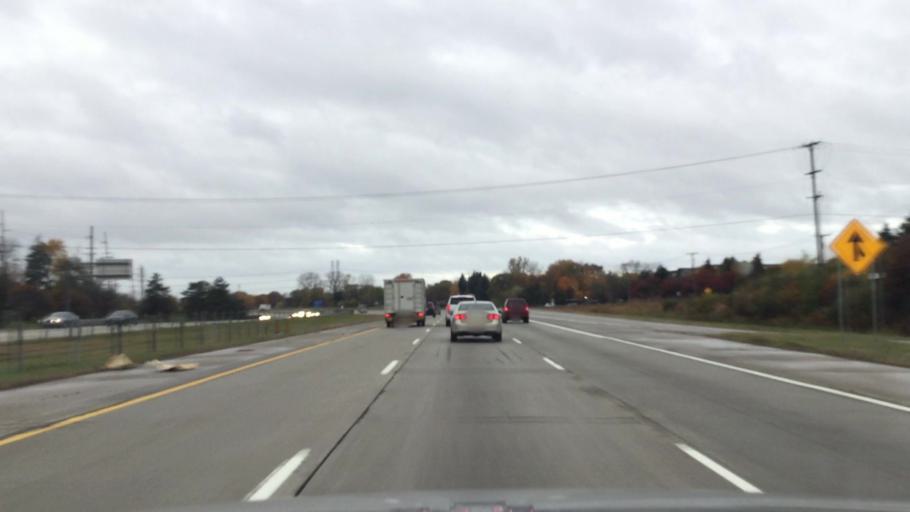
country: US
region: Michigan
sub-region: Wayne County
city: Belleville
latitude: 42.2208
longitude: -83.4439
